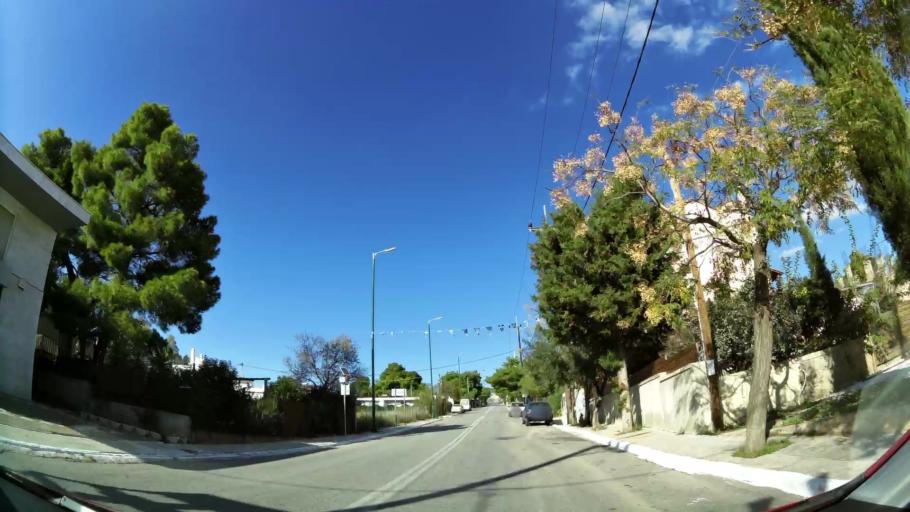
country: GR
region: Attica
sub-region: Nomarchia Anatolikis Attikis
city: Anthousa
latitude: 38.0276
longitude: 23.8737
